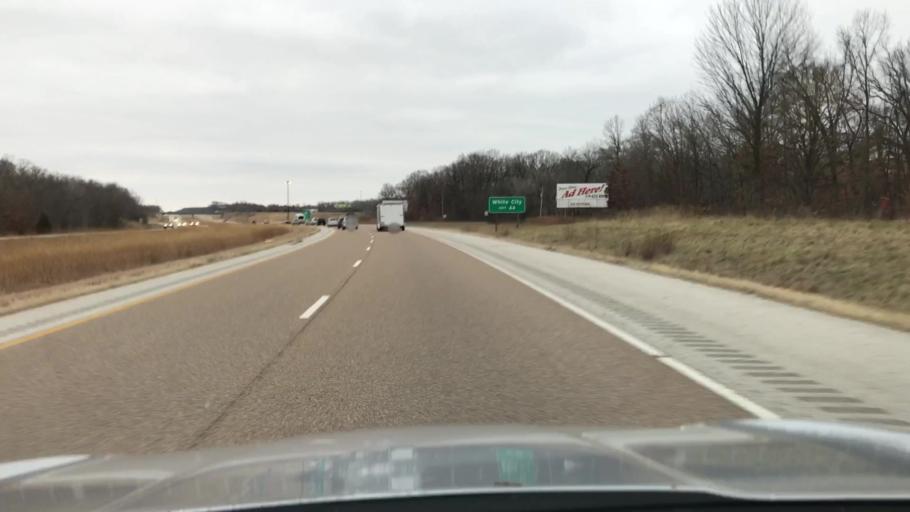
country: US
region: Illinois
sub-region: Macoupin County
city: Mount Olive
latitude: 39.0807
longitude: -89.7554
